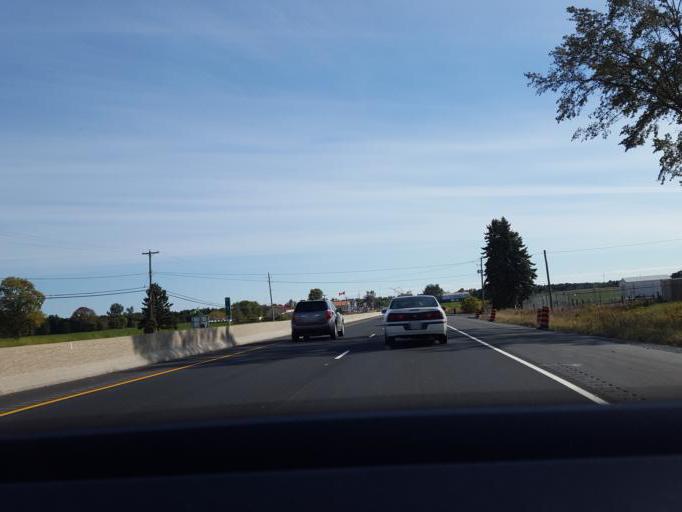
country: CA
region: Ontario
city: Oshawa
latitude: 43.9590
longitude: -78.6094
